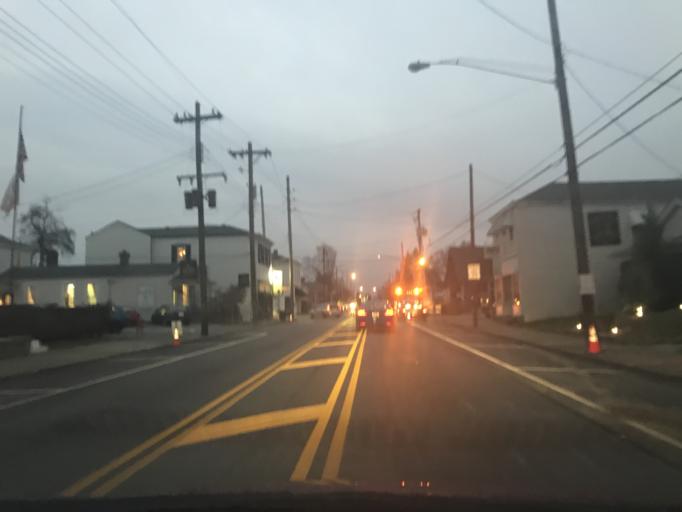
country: US
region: Kentucky
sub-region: Jefferson County
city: Audubon Park
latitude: 38.2275
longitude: -85.7359
